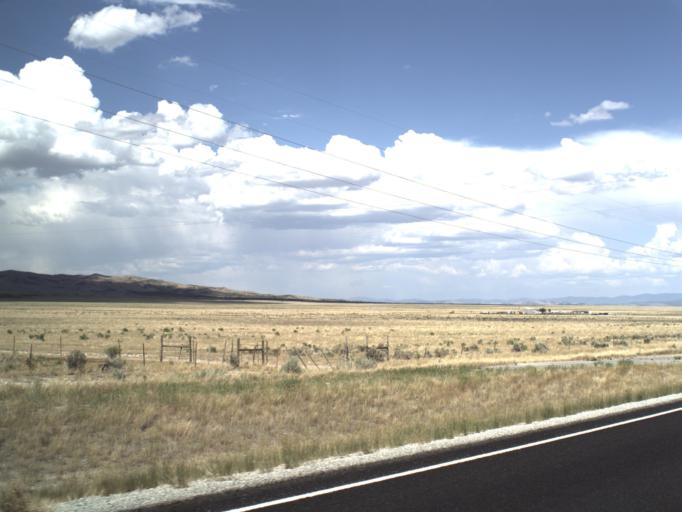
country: US
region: Idaho
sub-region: Minidoka County
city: Rupert
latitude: 41.9715
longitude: -113.1399
